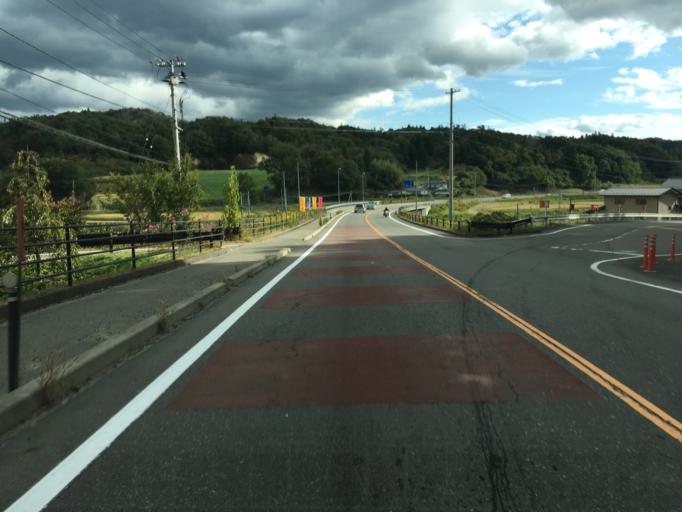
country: JP
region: Fukushima
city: Hobaramachi
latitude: 37.7738
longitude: 140.6093
